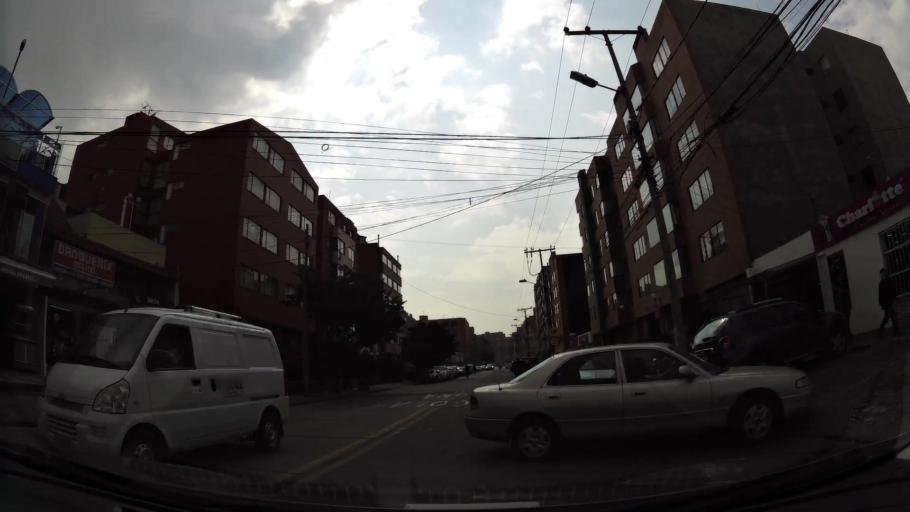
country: CO
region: Bogota D.C.
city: Barrio San Luis
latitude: 4.7323
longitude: -74.0518
